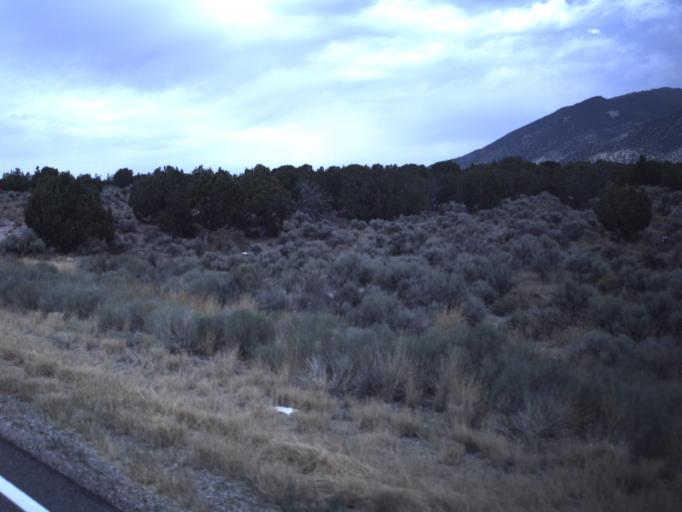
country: US
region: Utah
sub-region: Tooele County
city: Tooele
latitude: 40.3304
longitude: -112.2935
